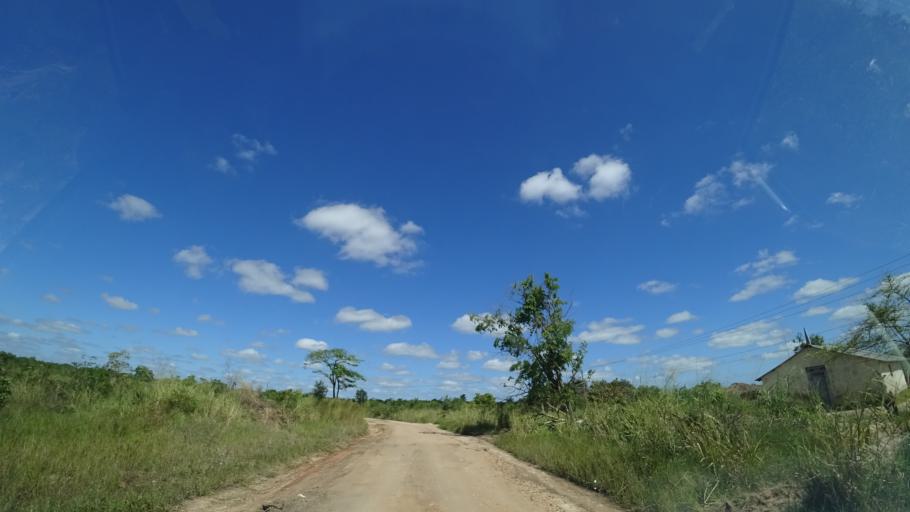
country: MZ
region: Sofala
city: Dondo
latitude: -19.3151
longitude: 34.6907
